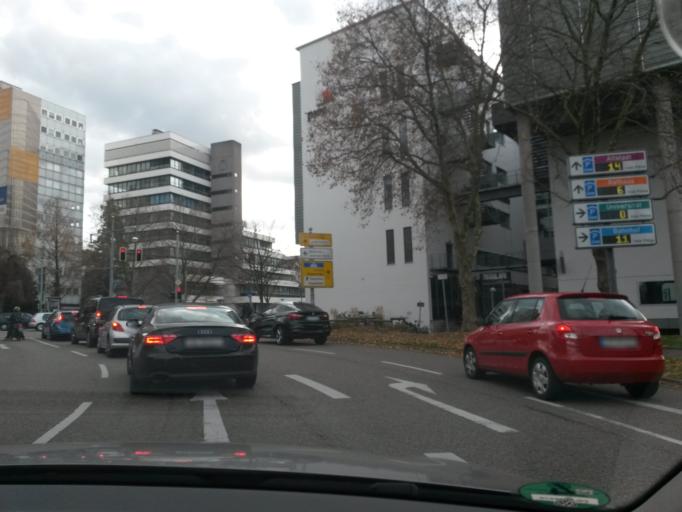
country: DE
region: Baden-Wuerttemberg
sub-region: Freiburg Region
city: Freiburg
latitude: 47.9998
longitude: 7.8434
